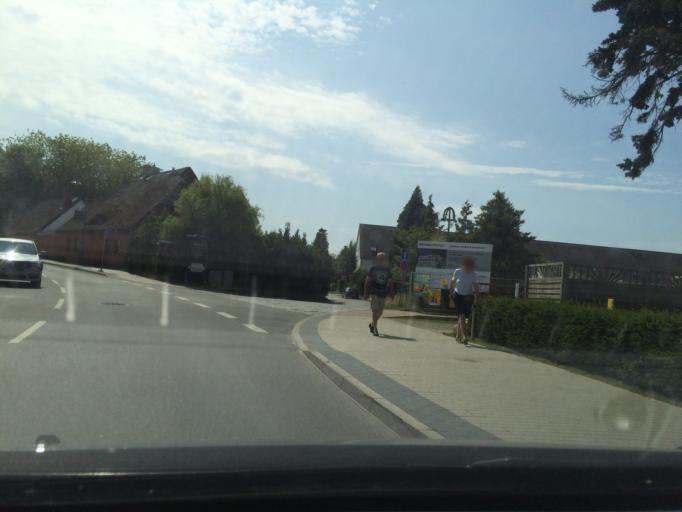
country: DE
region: Mecklenburg-Vorpommern
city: Ostseebad Binz
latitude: 54.3949
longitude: 13.6072
